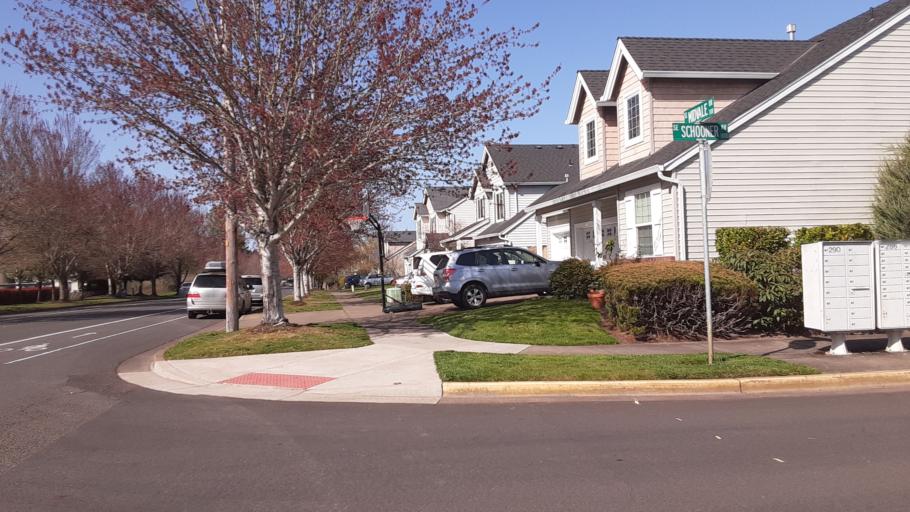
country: US
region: Oregon
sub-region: Benton County
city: Corvallis
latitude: 44.5333
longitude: -123.2565
